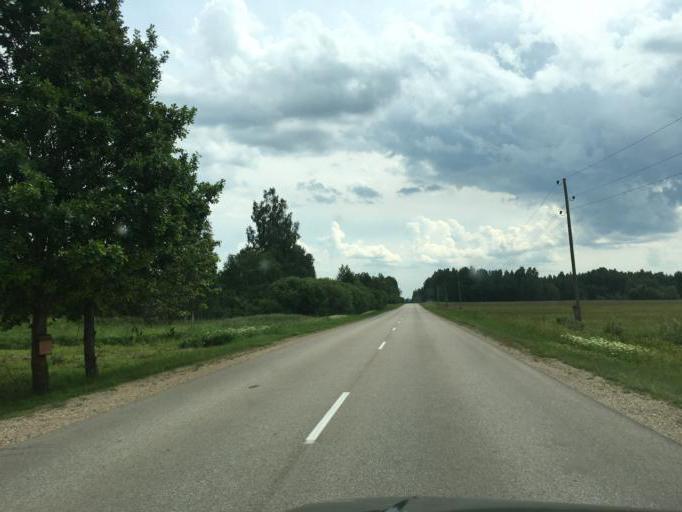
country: LV
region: Rugaju
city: Rugaji
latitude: 56.9567
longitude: 27.0673
